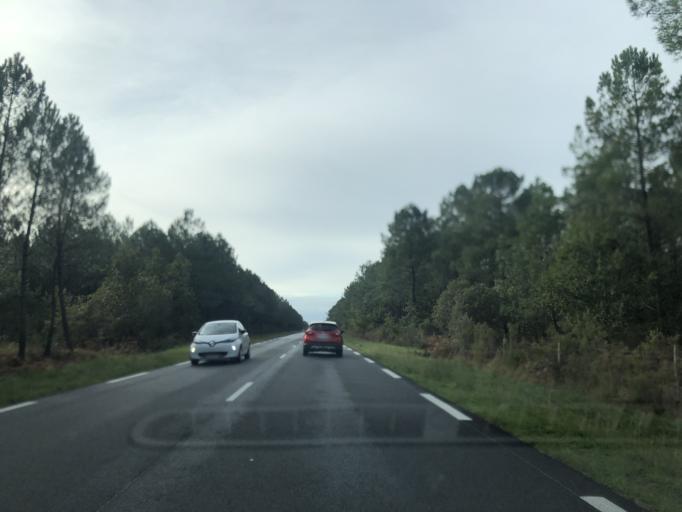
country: FR
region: Aquitaine
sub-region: Departement de la Gironde
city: Martignas-sur-Jalle
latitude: 44.8183
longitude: -0.8528
